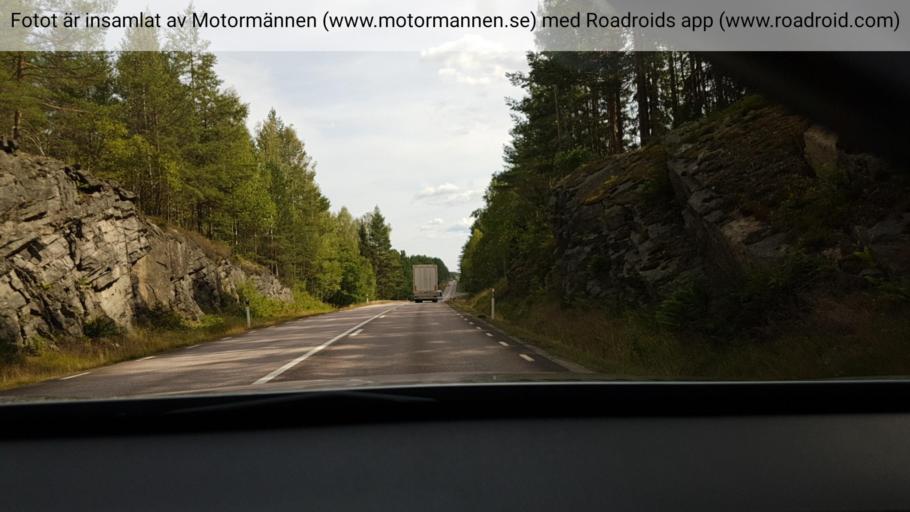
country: SE
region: Vaermland
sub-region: Karlstads Kommun
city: Edsvalla
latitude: 59.5943
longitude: 13.0077
